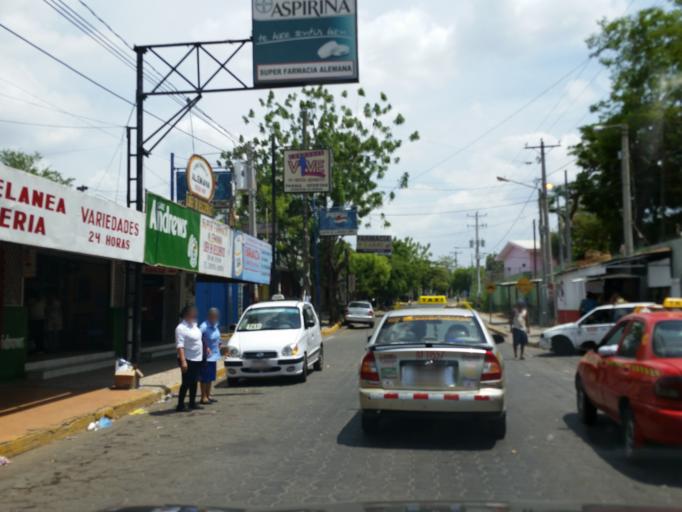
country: NI
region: Managua
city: Managua
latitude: 12.1474
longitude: -86.2179
